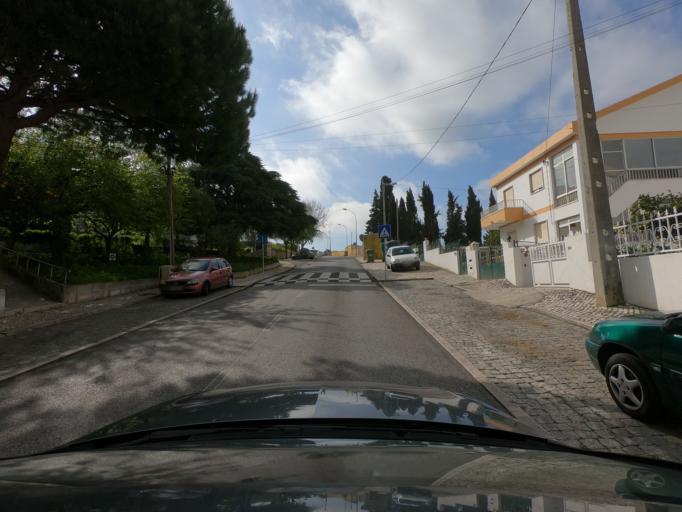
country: PT
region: Lisbon
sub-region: Oeiras
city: Barcarena
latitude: 38.7298
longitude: -9.2762
